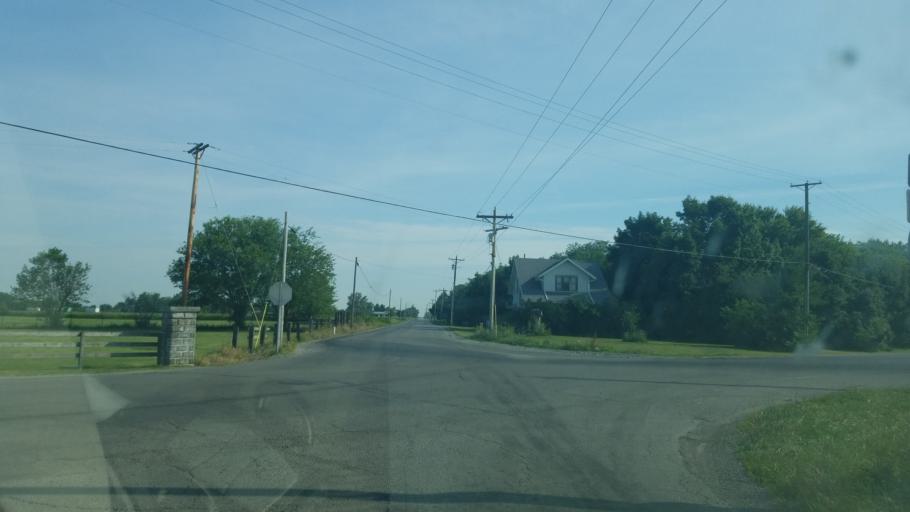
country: US
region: Ohio
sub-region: Hancock County
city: Findlay
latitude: 41.0034
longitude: -83.6985
